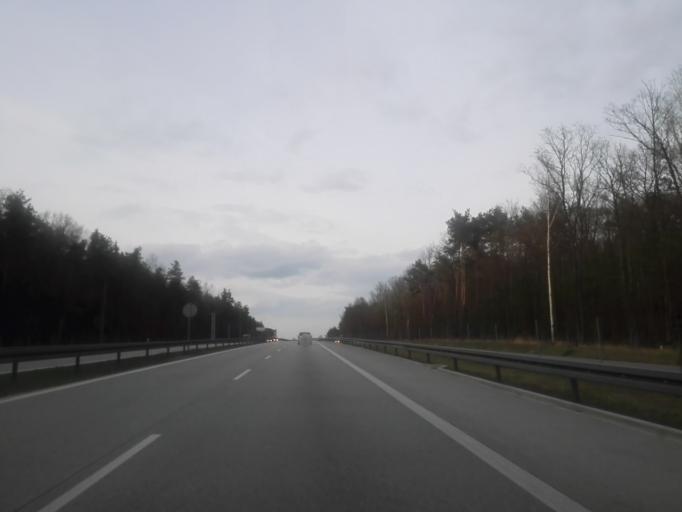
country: PL
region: Lodz Voivodeship
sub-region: Powiat tomaszowski
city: Lubochnia
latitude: 51.5817
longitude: 20.0320
